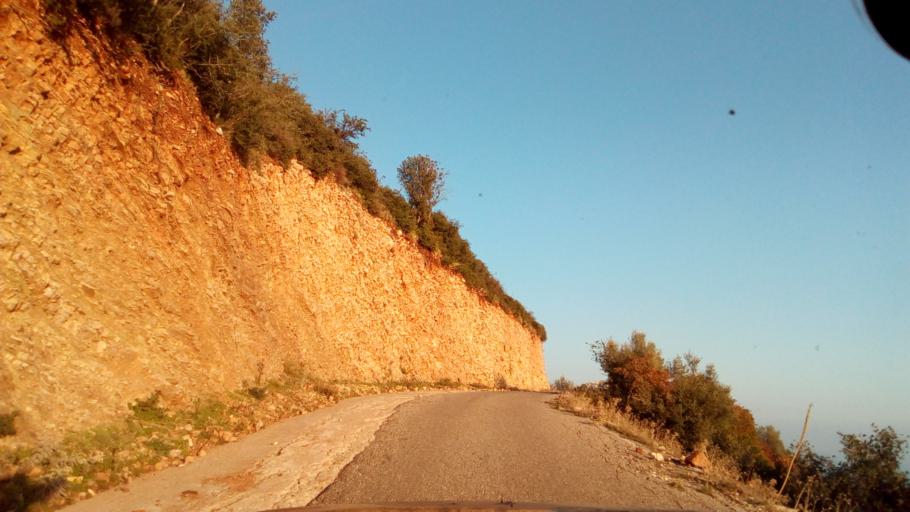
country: GR
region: West Greece
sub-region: Nomos Aitolias kai Akarnanias
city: Nafpaktos
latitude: 38.4272
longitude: 21.8508
